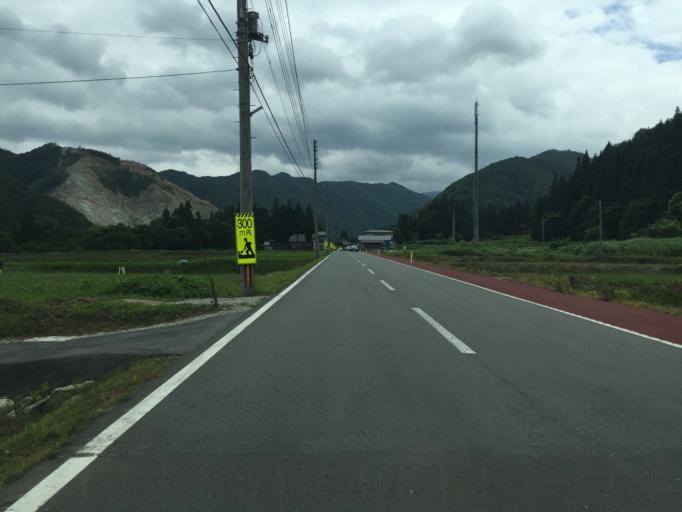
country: JP
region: Yamagata
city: Yonezawa
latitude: 37.8304
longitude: 140.0977
